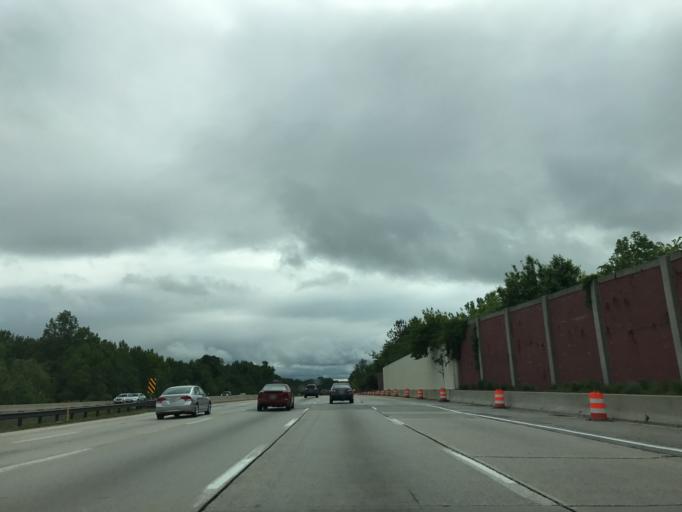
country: US
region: Maryland
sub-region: Prince George's County
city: Bowie
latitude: 38.9512
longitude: -76.7497
